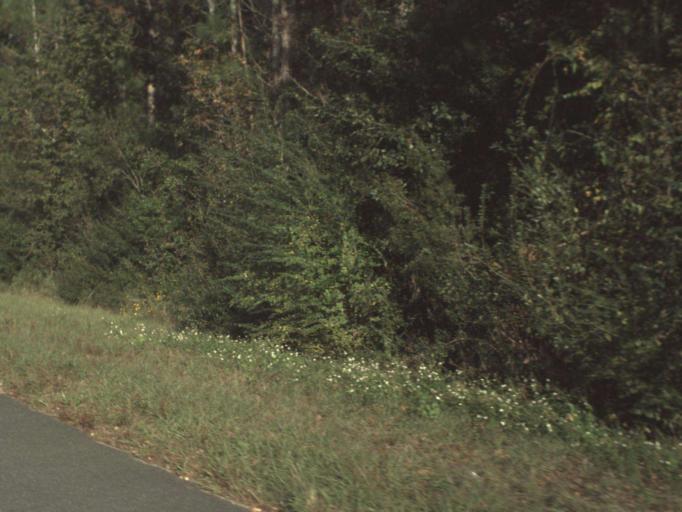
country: US
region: Florida
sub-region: Washington County
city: Chipley
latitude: 30.7390
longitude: -85.6050
